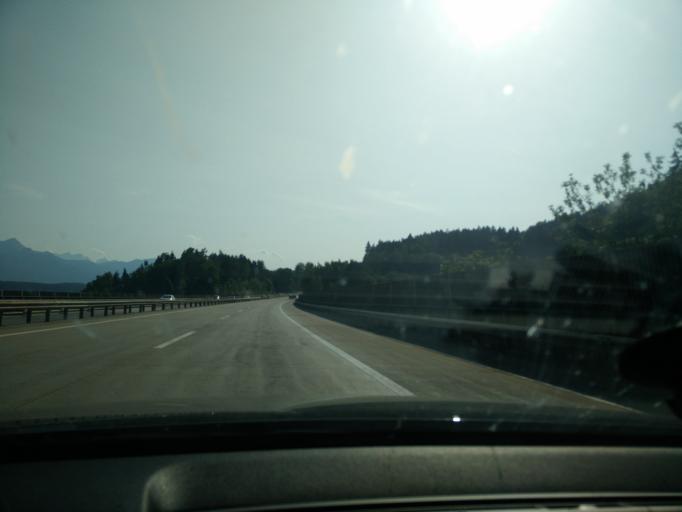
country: AT
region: Carinthia
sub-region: Politischer Bezirk Klagenfurt Land
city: Schiefling am See
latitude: 46.6353
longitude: 14.1108
